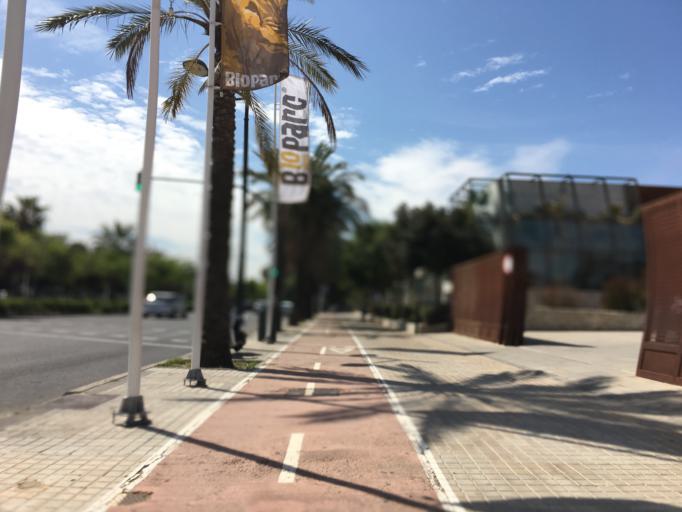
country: ES
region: Valencia
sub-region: Provincia de Valencia
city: Mislata
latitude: 39.4782
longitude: -0.4070
